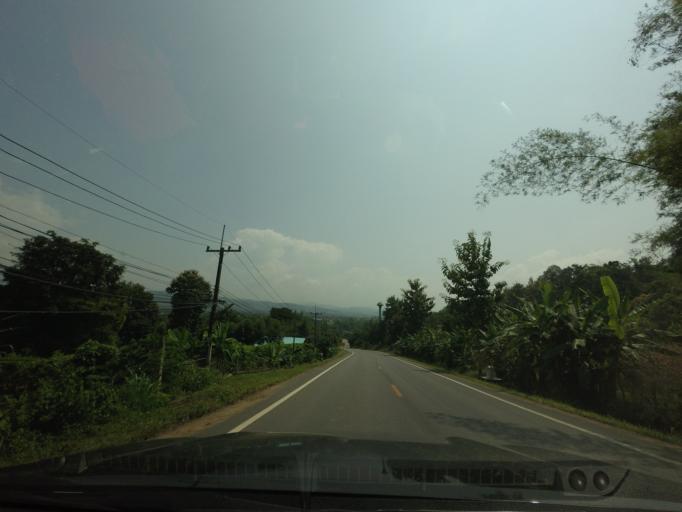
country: TH
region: Nan
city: Santi Suk
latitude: 18.9240
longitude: 100.9210
